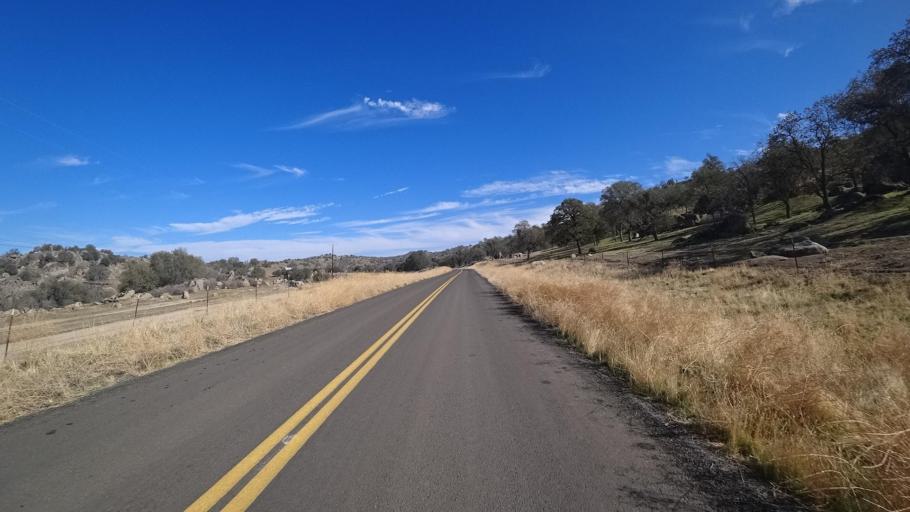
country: US
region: California
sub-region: Kern County
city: Oildale
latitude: 35.6332
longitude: -118.8424
